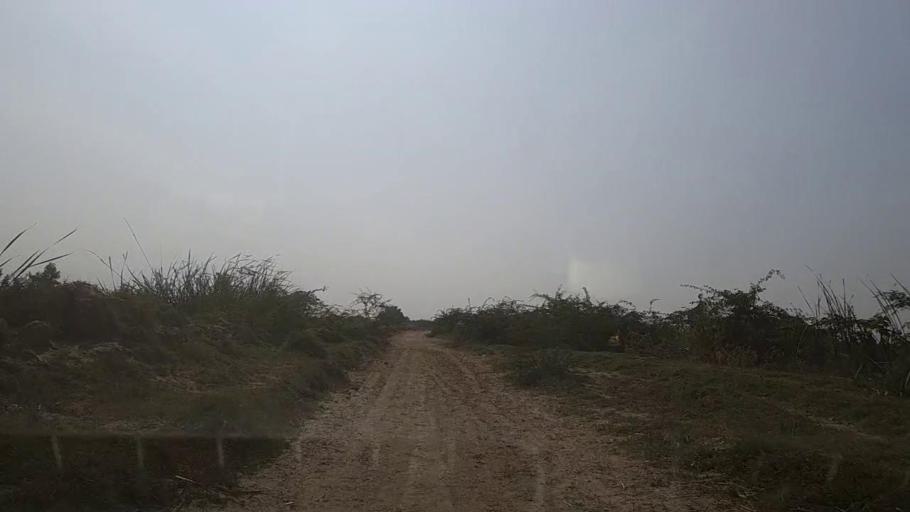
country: PK
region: Sindh
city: Mirpur Sakro
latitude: 24.5469
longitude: 67.7901
